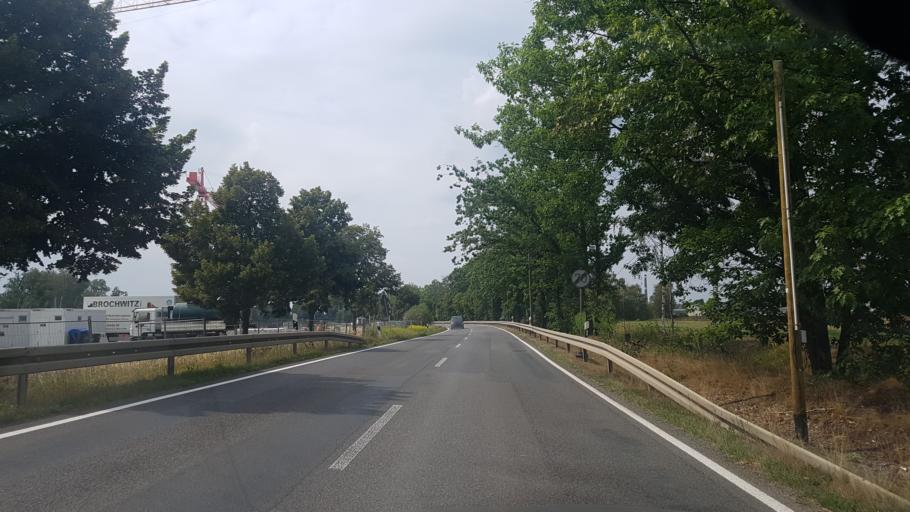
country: DE
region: Brandenburg
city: Plessa
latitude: 51.4671
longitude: 13.6410
